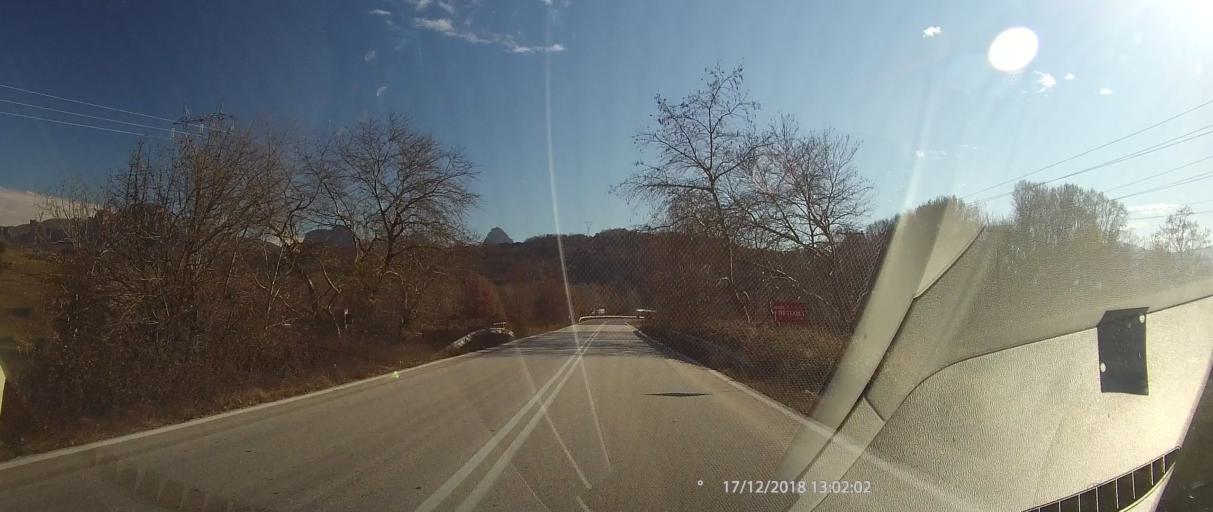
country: GR
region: Thessaly
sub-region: Trikala
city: Kastraki
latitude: 39.7287
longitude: 21.5915
